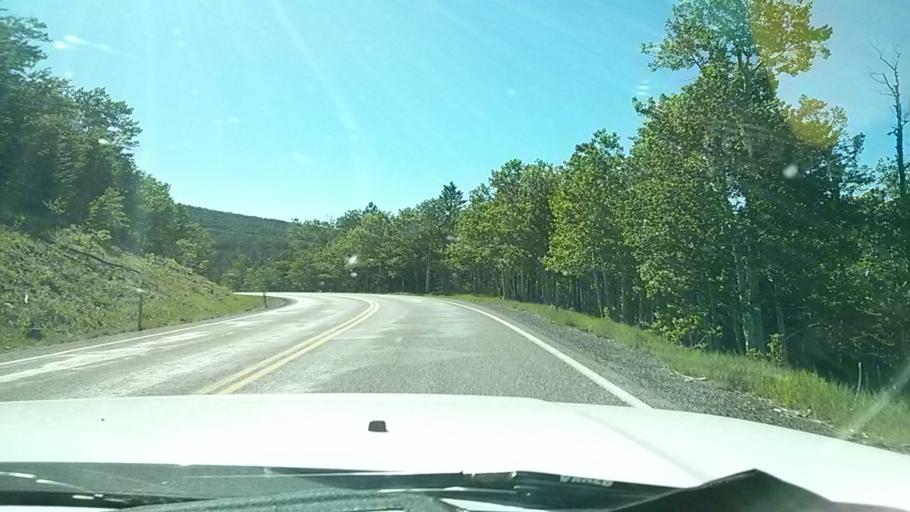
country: US
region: Utah
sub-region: Wayne County
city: Loa
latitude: 38.0861
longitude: -111.3380
